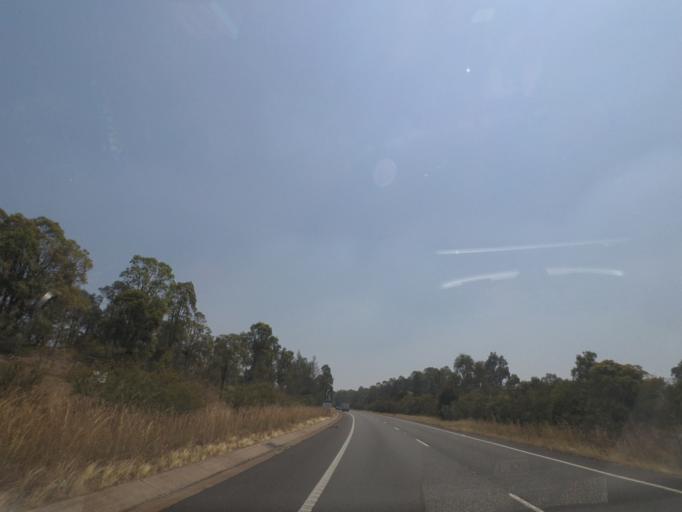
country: AU
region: New South Wales
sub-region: Newcastle
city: Beresfield
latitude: -32.8371
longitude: 151.6349
